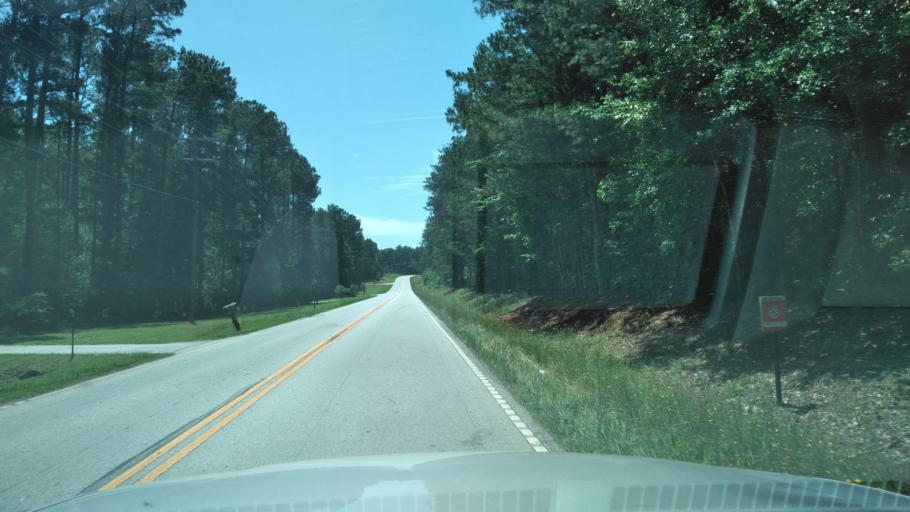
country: US
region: South Carolina
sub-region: Laurens County
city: Laurens
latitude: 34.4993
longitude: -82.0583
